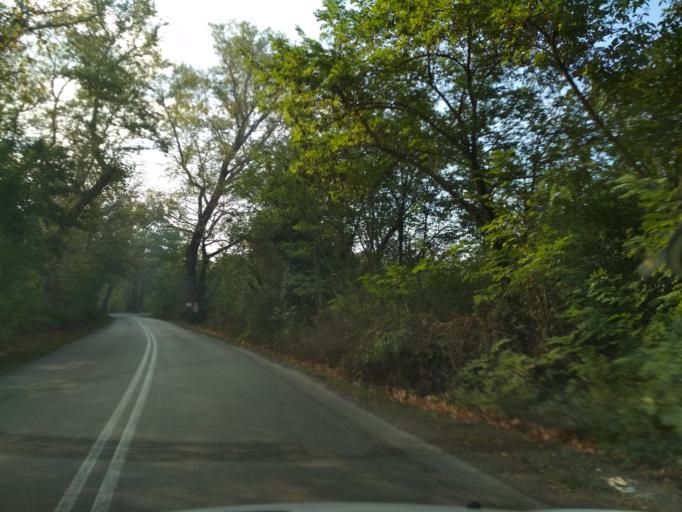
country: GR
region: Central Greece
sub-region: Nomos Evvoias
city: Prokopion
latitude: 38.7411
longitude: 23.4905
